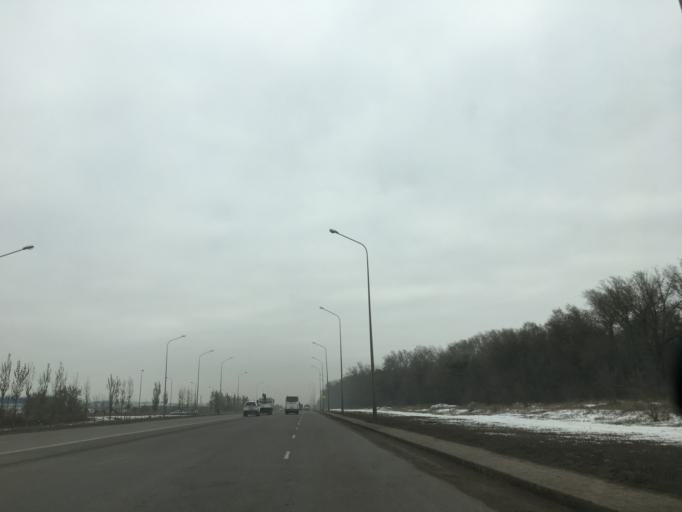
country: KZ
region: Astana Qalasy
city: Astana
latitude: 51.1690
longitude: 71.4952
